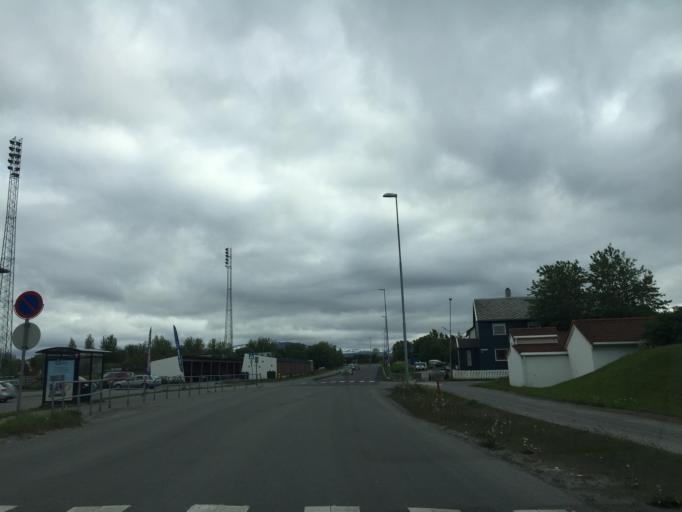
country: NO
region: Nordland
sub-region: Bodo
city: Bodo
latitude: 67.2765
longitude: 14.3820
